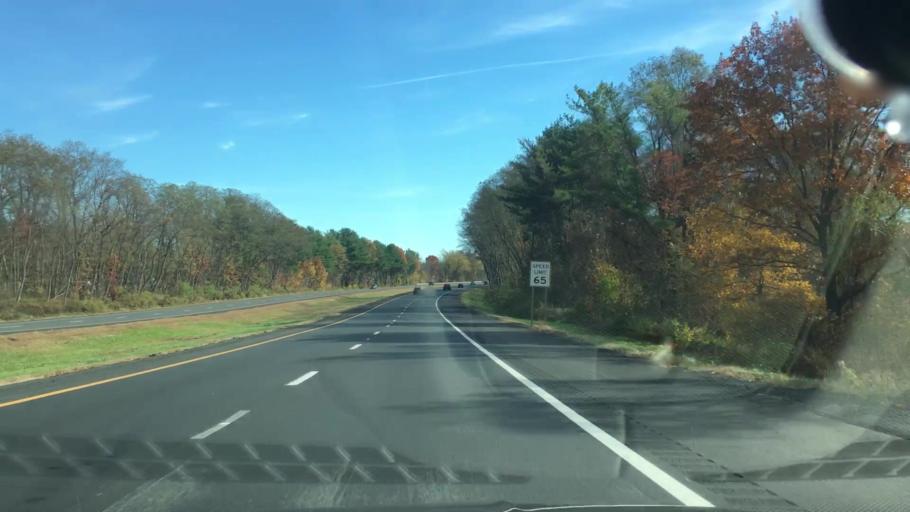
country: US
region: Massachusetts
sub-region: Hampshire County
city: Northampton
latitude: 42.3375
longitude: -72.6304
